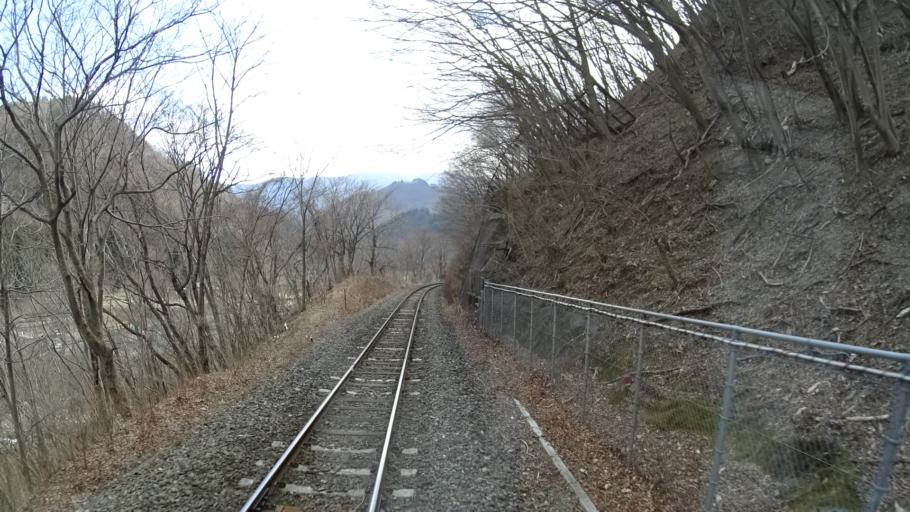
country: JP
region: Iwate
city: Kamaishi
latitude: 39.2706
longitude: 141.7253
